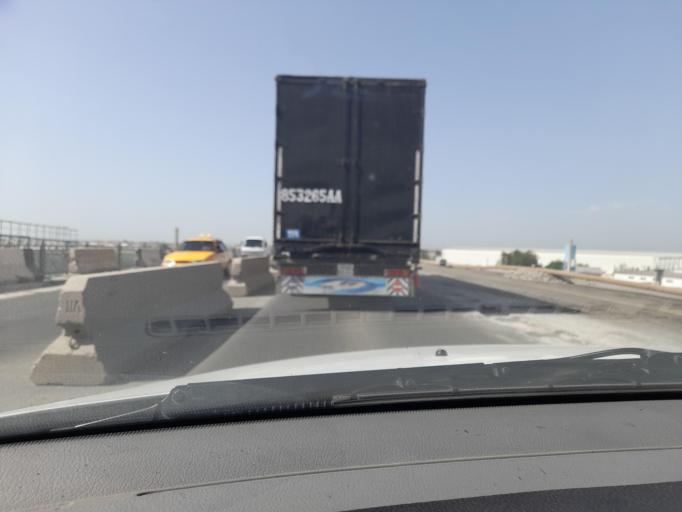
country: UZ
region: Samarqand
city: Samarqand
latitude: 39.6962
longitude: 67.0189
